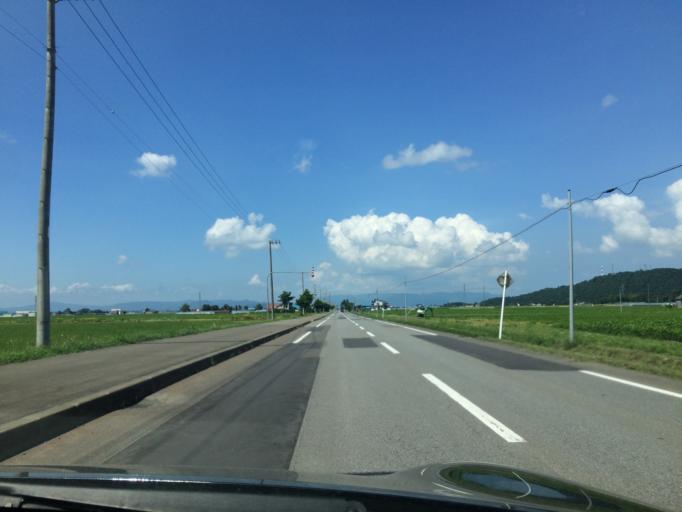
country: JP
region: Hokkaido
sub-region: Asahikawa-shi
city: Asahikawa
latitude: 43.7470
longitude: 142.4618
